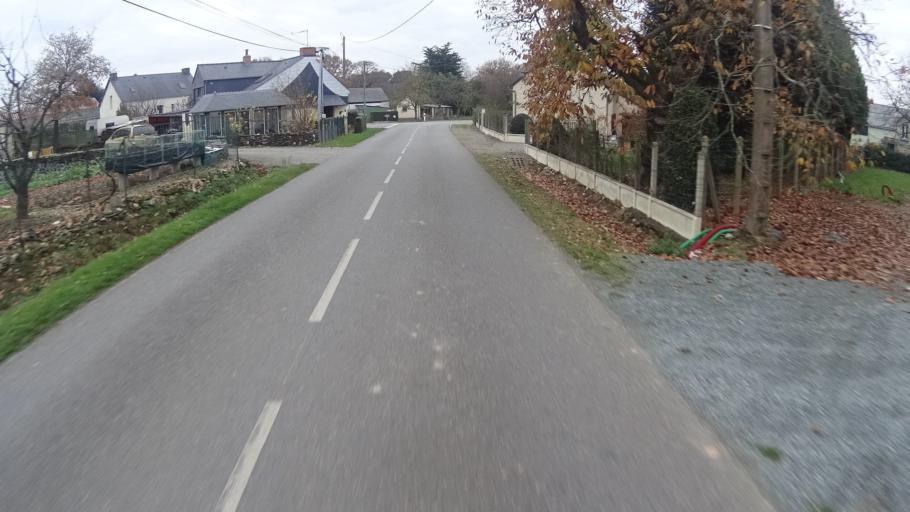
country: FR
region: Pays de la Loire
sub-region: Departement de la Loire-Atlantique
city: Avessac
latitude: 47.6676
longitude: -1.9238
